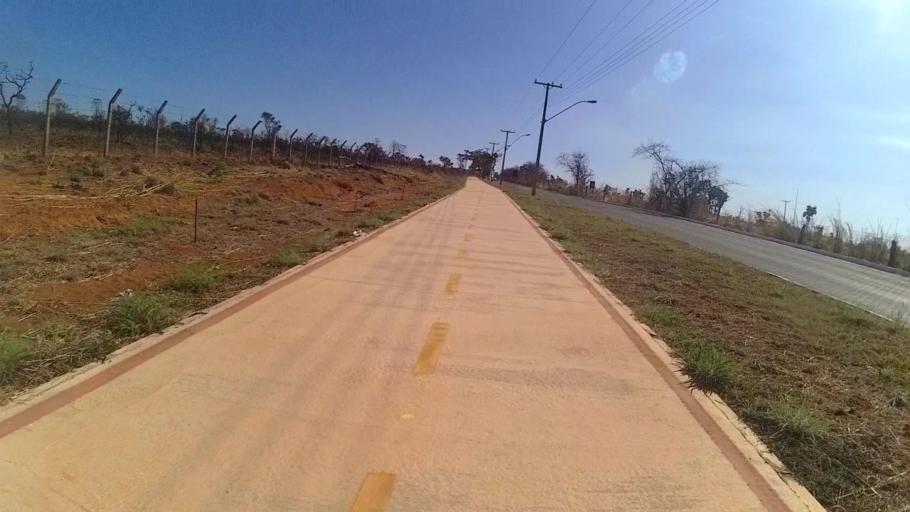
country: BR
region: Federal District
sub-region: Brasilia
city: Brasilia
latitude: -15.6544
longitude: -47.8954
